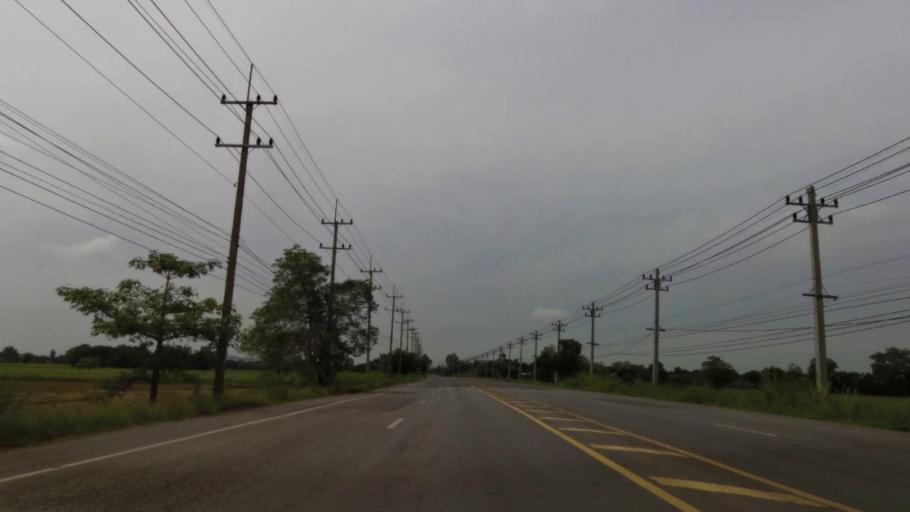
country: TH
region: Lop Buri
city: Ban Mi
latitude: 15.0584
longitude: 100.5930
